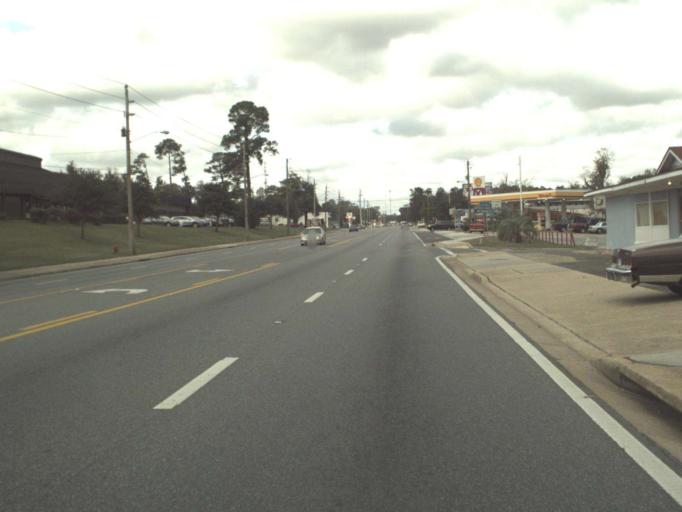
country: US
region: Florida
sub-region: Santa Rosa County
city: Milton
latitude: 30.6316
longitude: -87.0431
